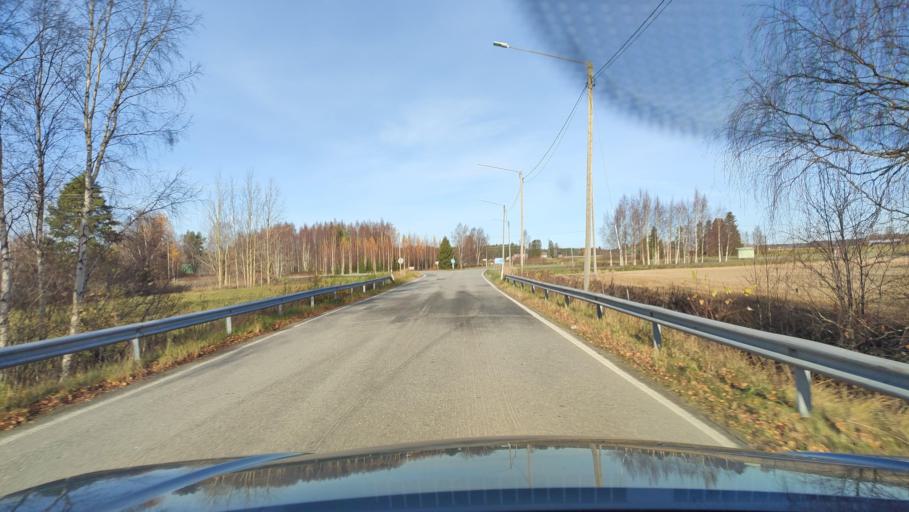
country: FI
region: Southern Ostrobothnia
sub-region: Suupohja
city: Teuva
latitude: 62.4596
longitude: 21.6044
